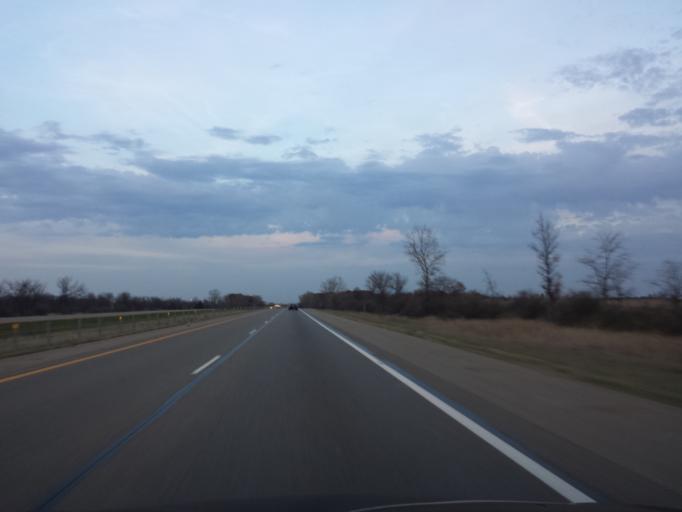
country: US
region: Michigan
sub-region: Shiawassee County
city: Durand
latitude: 42.9124
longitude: -84.0445
